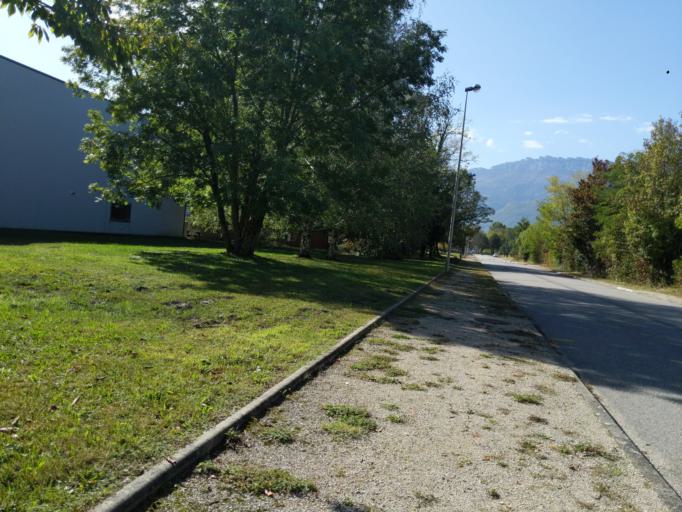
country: FR
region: Rhone-Alpes
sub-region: Departement de la Savoie
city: Montmelian
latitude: 45.4779
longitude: 6.0358
